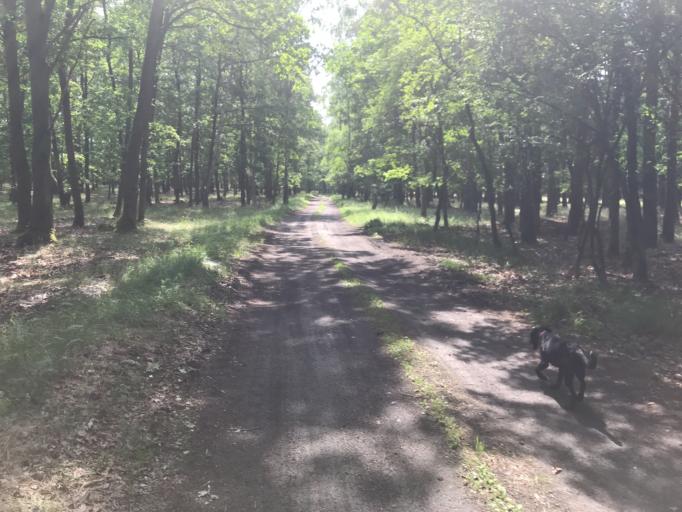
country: PL
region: West Pomeranian Voivodeship
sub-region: Powiat mysliborski
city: Boleszkowice
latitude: 52.6928
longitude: 14.4915
